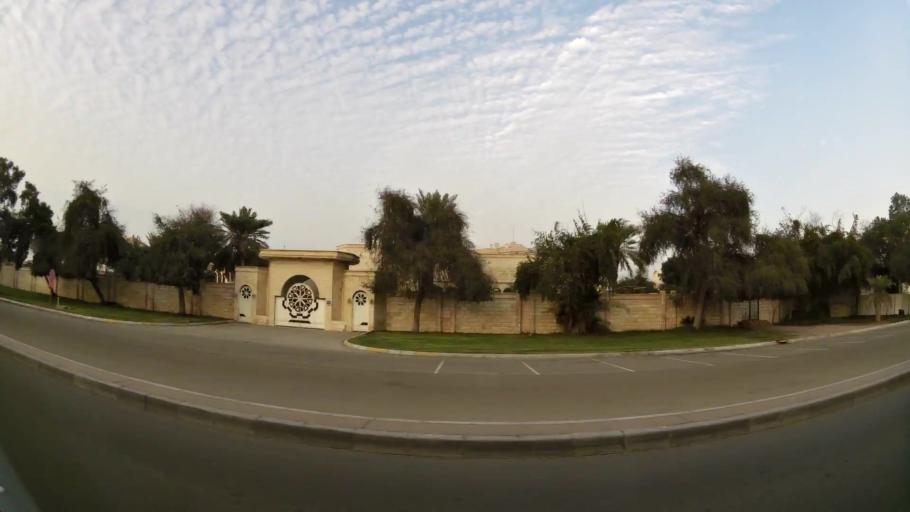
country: AE
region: Abu Dhabi
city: Abu Dhabi
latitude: 24.4349
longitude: 54.3817
